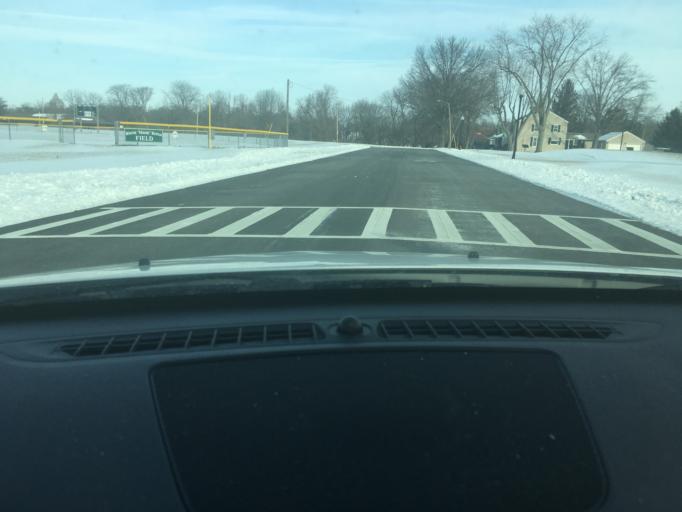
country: US
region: Illinois
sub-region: LaSalle County
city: Peru
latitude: 41.3326
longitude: -89.1228
